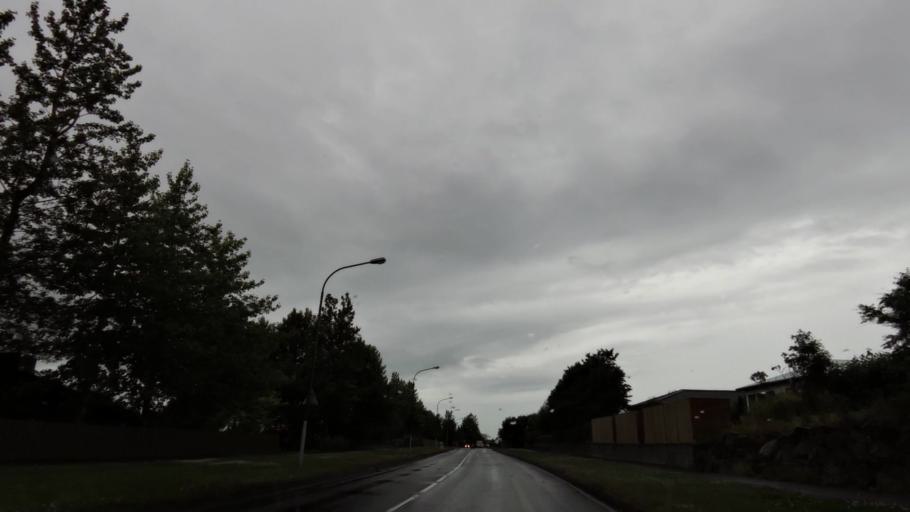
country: IS
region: Capital Region
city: Reykjavik
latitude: 64.1358
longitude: -21.8026
